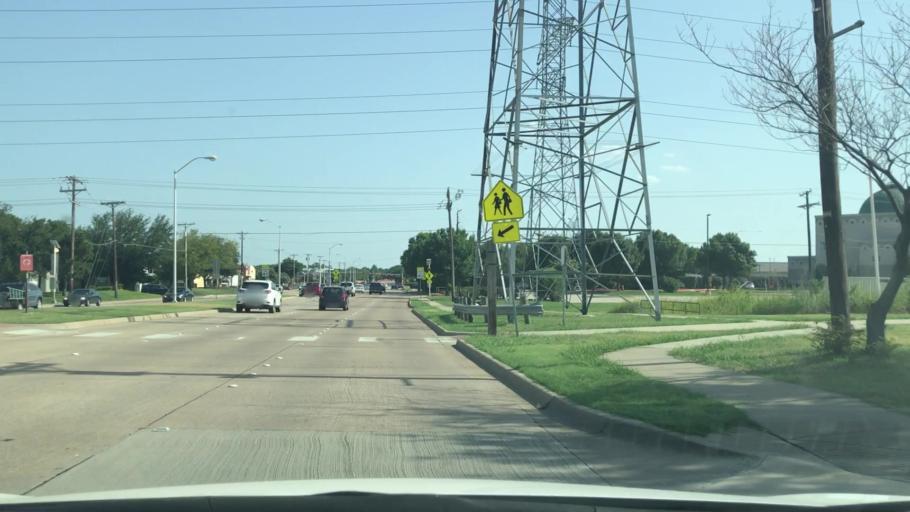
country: US
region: Texas
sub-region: Collin County
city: Plano
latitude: 33.0610
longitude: -96.7505
